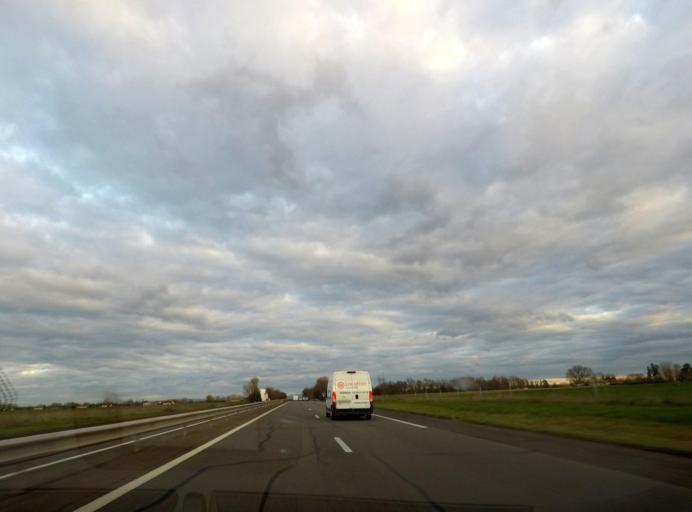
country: FR
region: Rhone-Alpes
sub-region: Departement de l'Ain
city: Saint-Cyr-sur-Menthon
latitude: 46.2822
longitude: 4.9601
